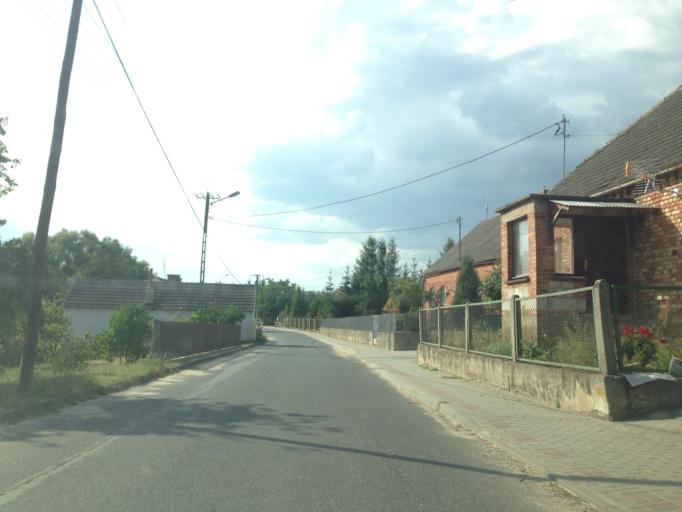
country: PL
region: Kujawsko-Pomorskie
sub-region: Powiat swiecki
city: Swiekatowo
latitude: 53.4907
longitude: 18.1370
